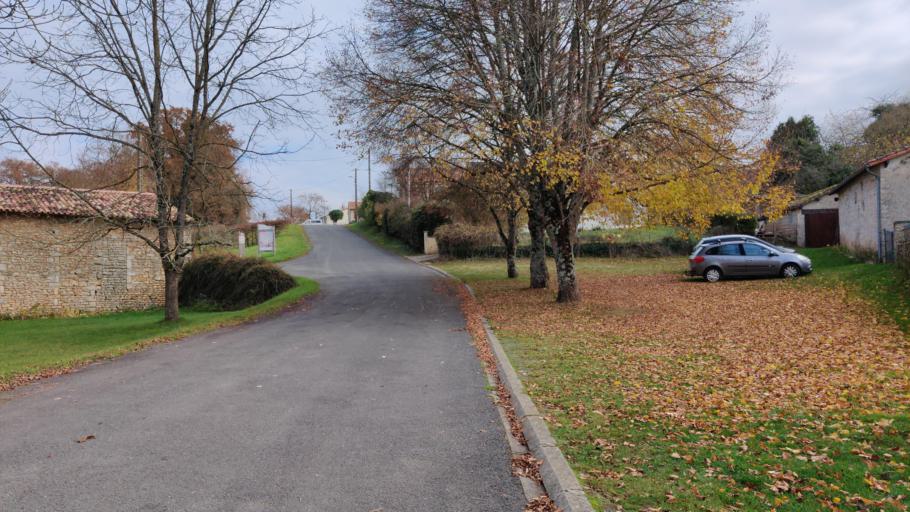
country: FR
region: Poitou-Charentes
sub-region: Departement de la Vienne
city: Rouille
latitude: 46.4642
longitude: 0.0713
